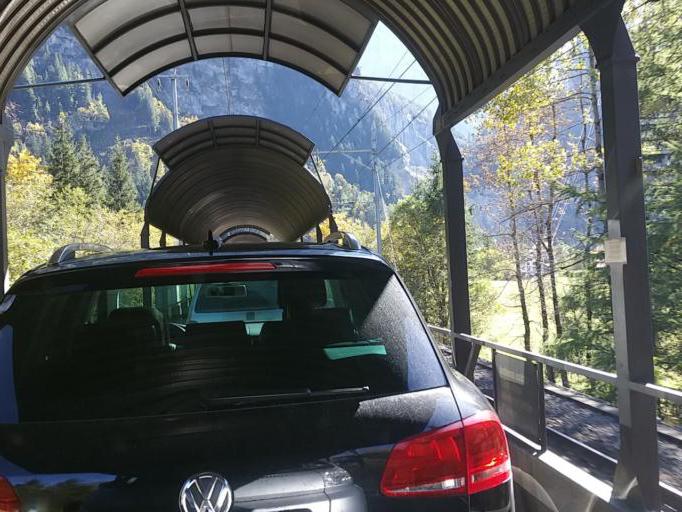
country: CH
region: Bern
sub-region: Frutigen-Niedersimmental District
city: Kandersteg
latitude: 46.4821
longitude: 7.6657
